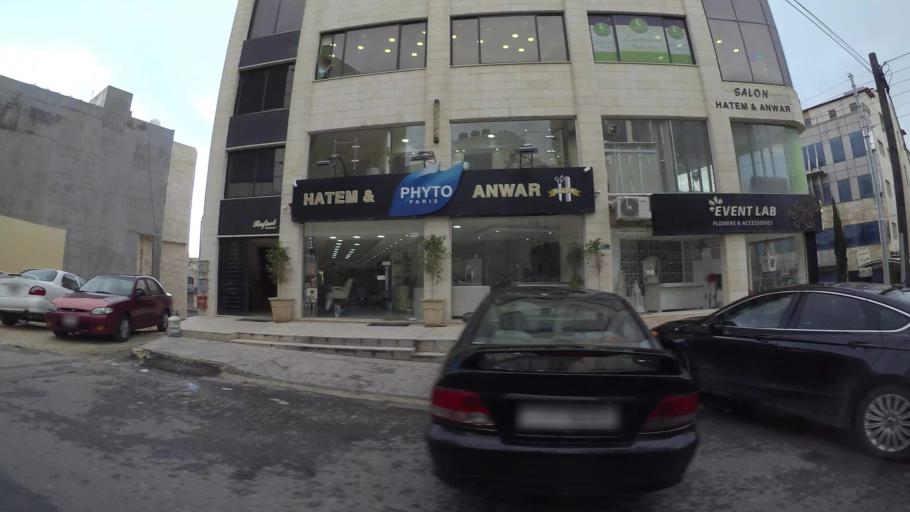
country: JO
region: Amman
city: Wadi as Sir
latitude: 31.9505
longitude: 35.8718
